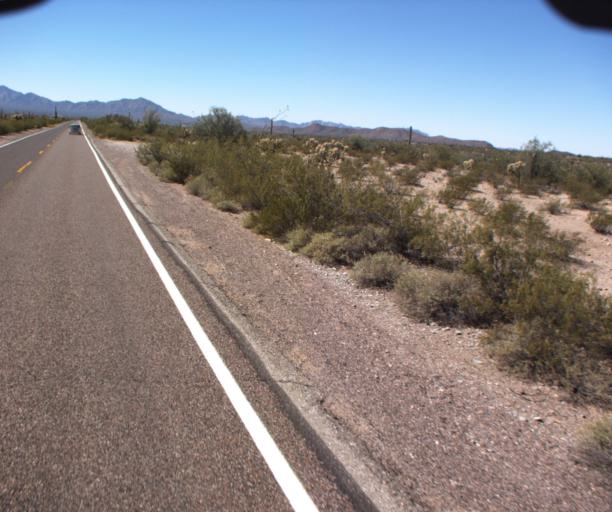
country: MX
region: Sonora
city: Sonoyta
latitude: 31.9286
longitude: -112.8018
